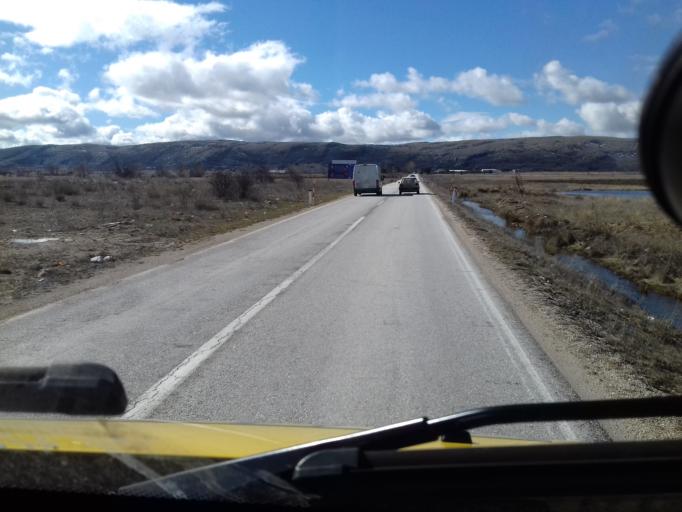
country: BA
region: Federation of Bosnia and Herzegovina
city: Tomislavgrad
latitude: 43.6934
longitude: 17.2111
